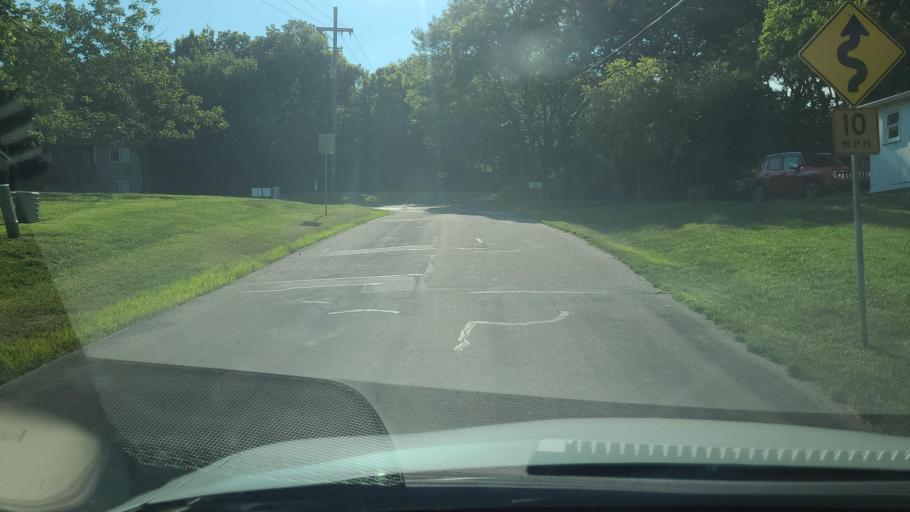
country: US
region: Kansas
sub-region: Douglas County
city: Lawrence
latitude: 38.9751
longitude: -95.2572
